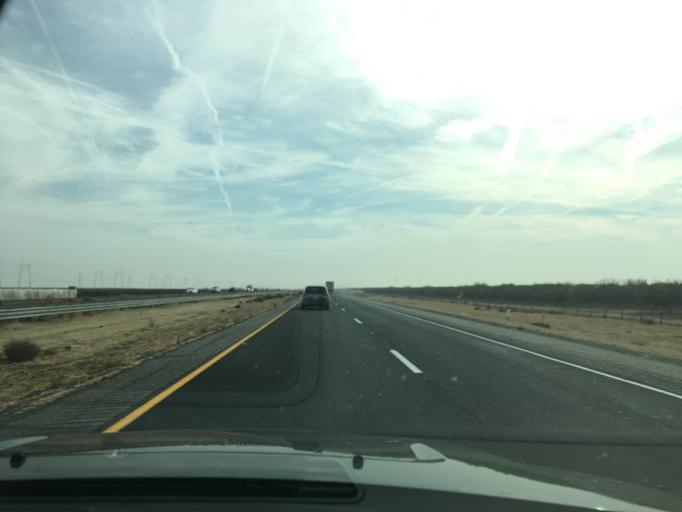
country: US
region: California
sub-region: Kings County
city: Kettleman City
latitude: 35.8703
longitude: -119.8479
